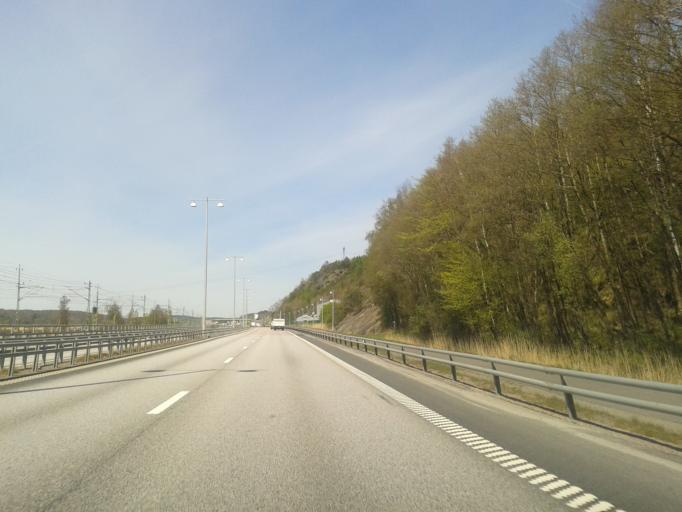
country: SE
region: Vaestra Goetaland
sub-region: Goteborg
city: Gardsten
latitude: 57.8087
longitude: 12.0163
